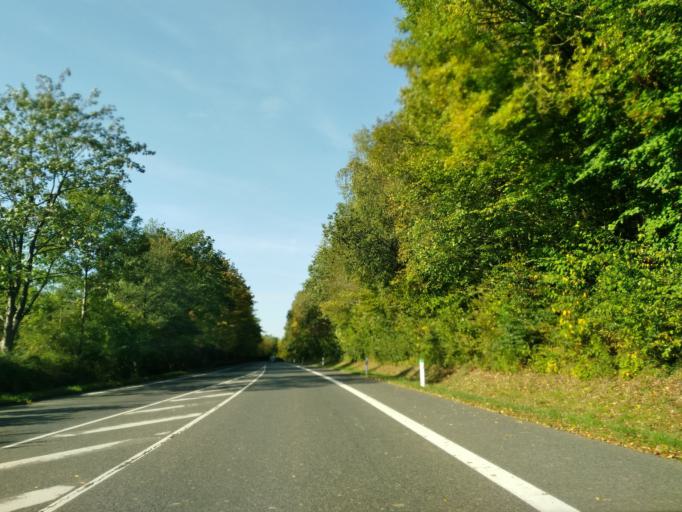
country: DE
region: North Rhine-Westphalia
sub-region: Regierungsbezirk Koln
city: Hennef
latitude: 50.7061
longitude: 7.2877
